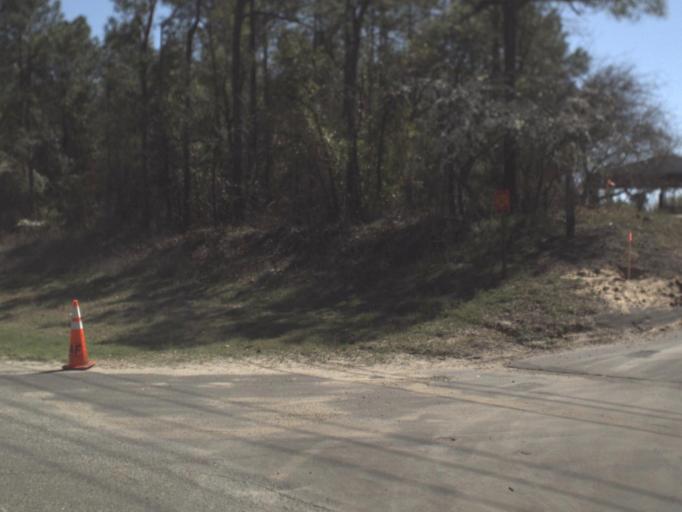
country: US
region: Florida
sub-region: Leon County
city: Tallahassee
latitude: 30.3858
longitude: -84.3110
